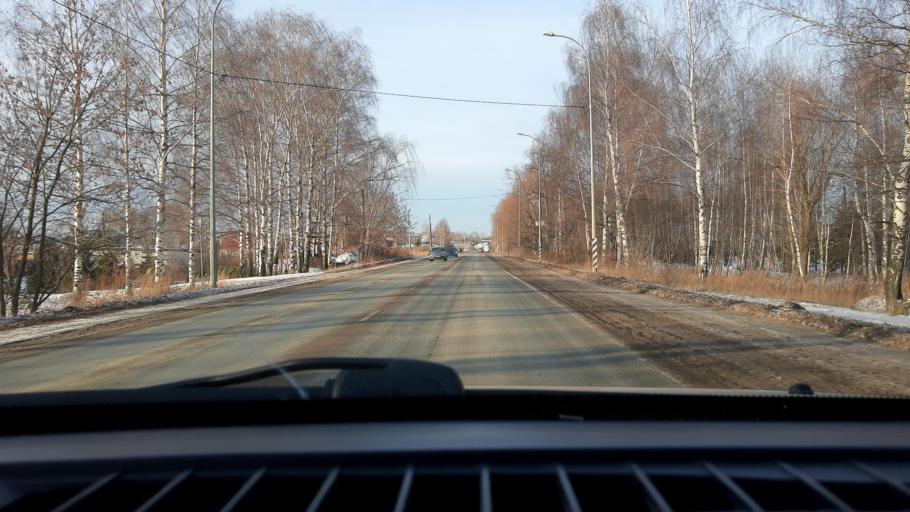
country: RU
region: Nizjnij Novgorod
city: Bor
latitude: 56.3786
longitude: 44.0488
